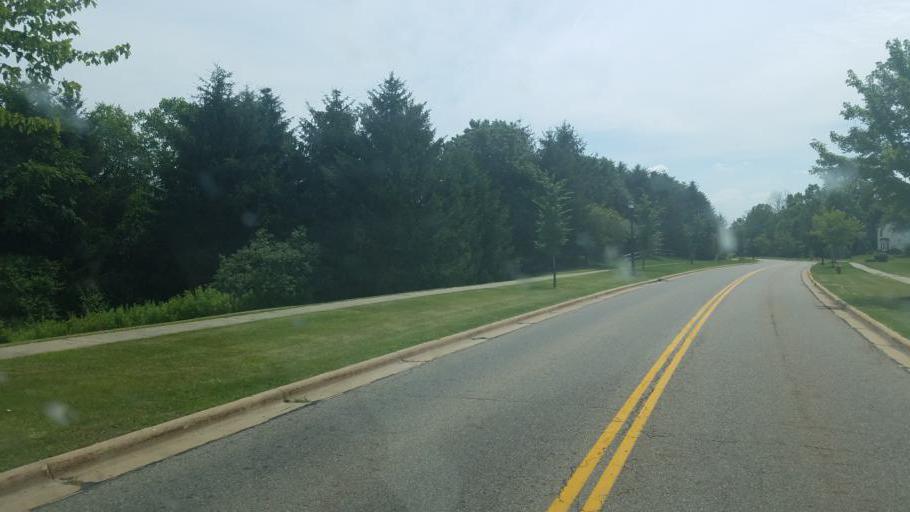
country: US
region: Ohio
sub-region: Summit County
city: Twinsburg
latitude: 41.3401
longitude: -81.4341
